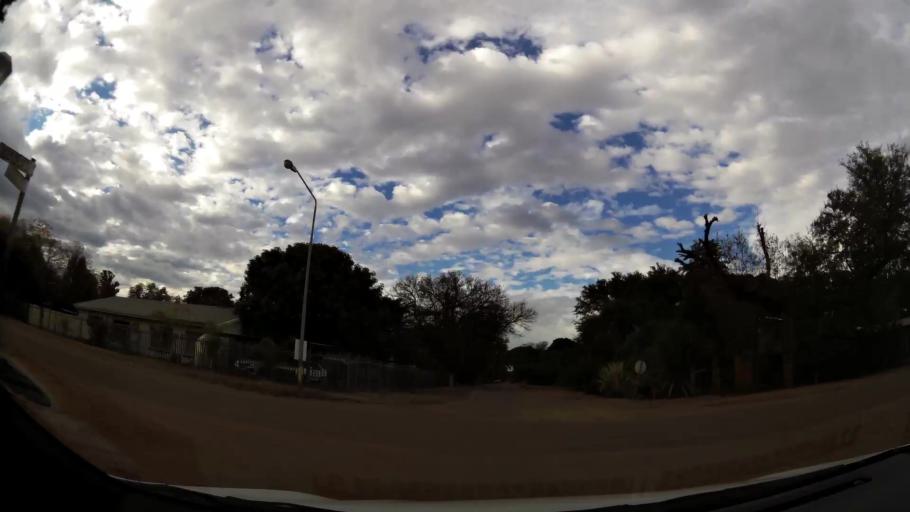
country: ZA
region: Limpopo
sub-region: Waterberg District Municipality
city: Modimolle
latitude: -24.5118
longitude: 28.7119
